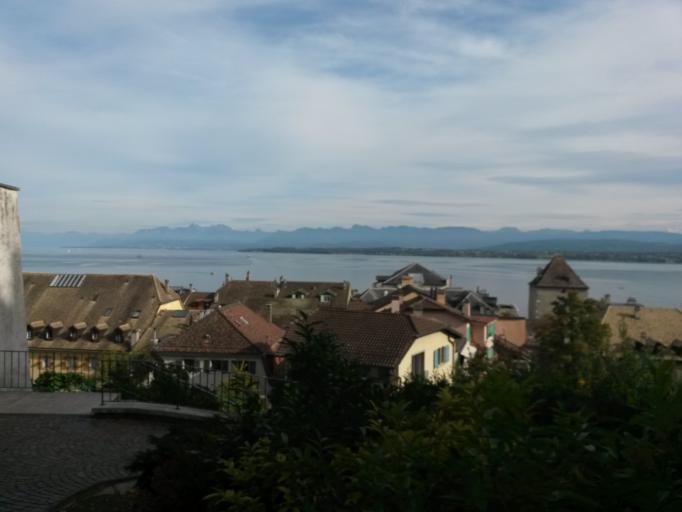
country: CH
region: Vaud
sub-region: Nyon District
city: Nyon
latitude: 46.3818
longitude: 6.2407
